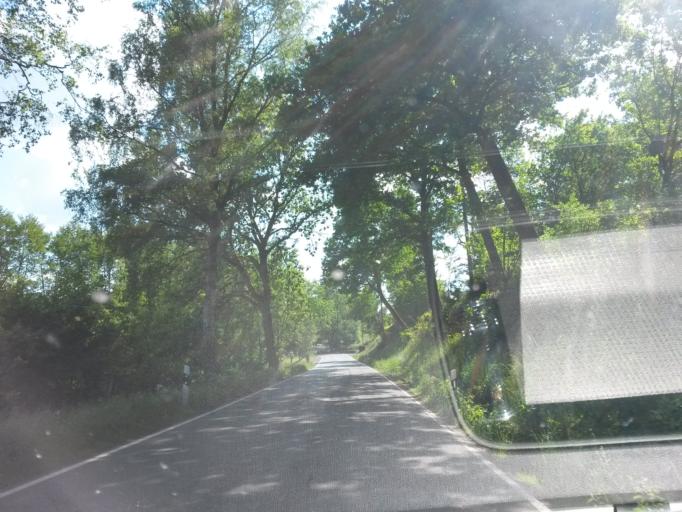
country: DE
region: North Rhine-Westphalia
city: Balve
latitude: 51.2886
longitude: 7.8481
